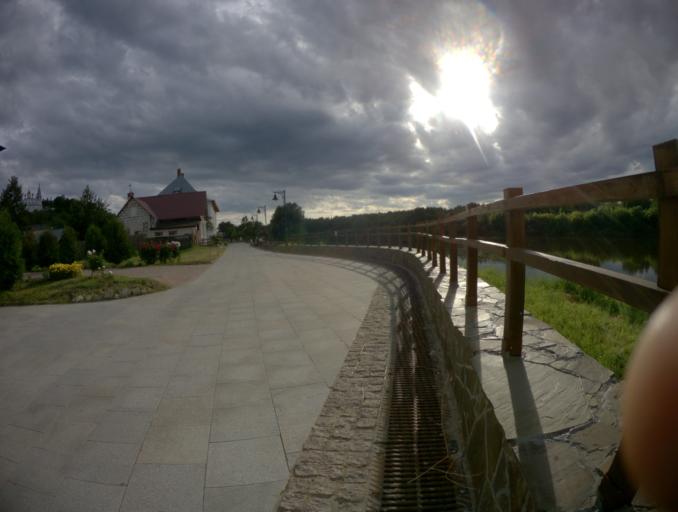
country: RU
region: Vladimir
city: Gorokhovets
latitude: 56.2078
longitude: 42.6756
